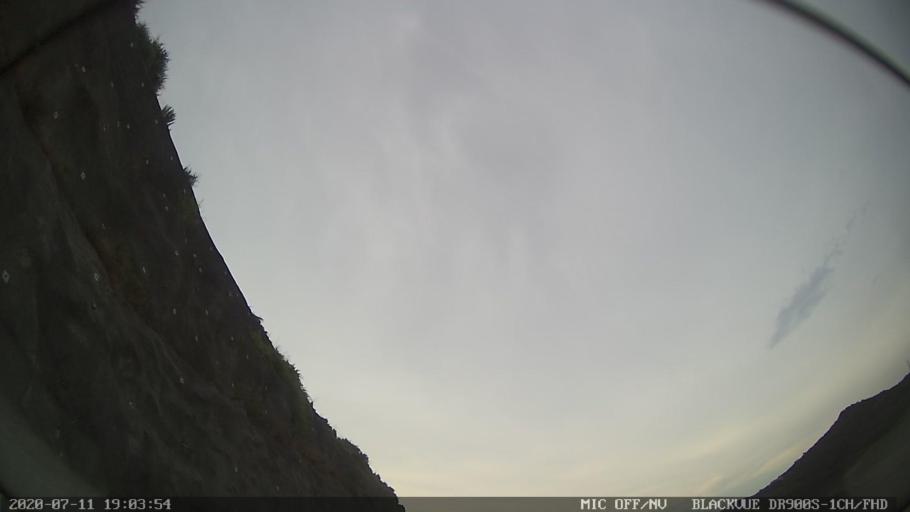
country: PT
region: Vila Real
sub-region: Peso da Regua
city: Peso da Regua
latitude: 41.1778
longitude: -7.7494
